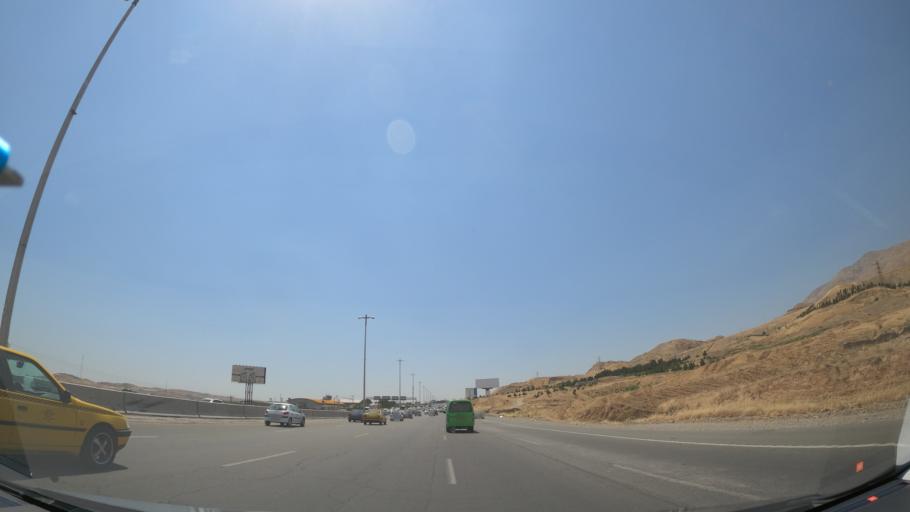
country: IR
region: Tehran
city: Shahr-e Qods
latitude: 35.7428
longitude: 51.1085
